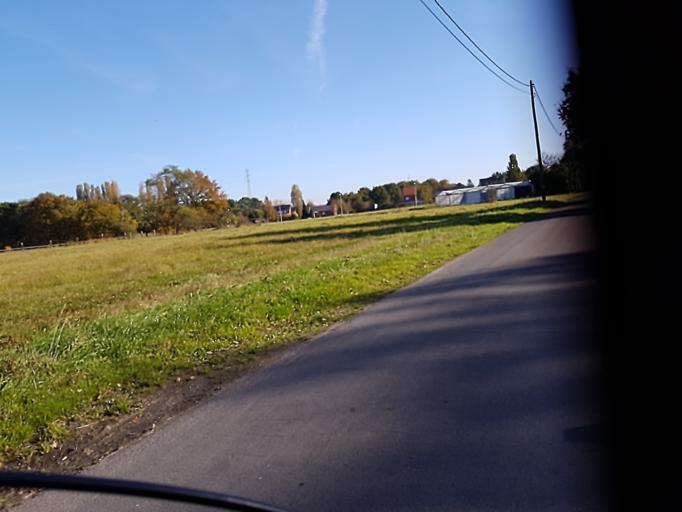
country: BE
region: Flanders
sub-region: Provincie Antwerpen
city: Sint-Katelijne-Waver
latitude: 51.0814
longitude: 4.5365
